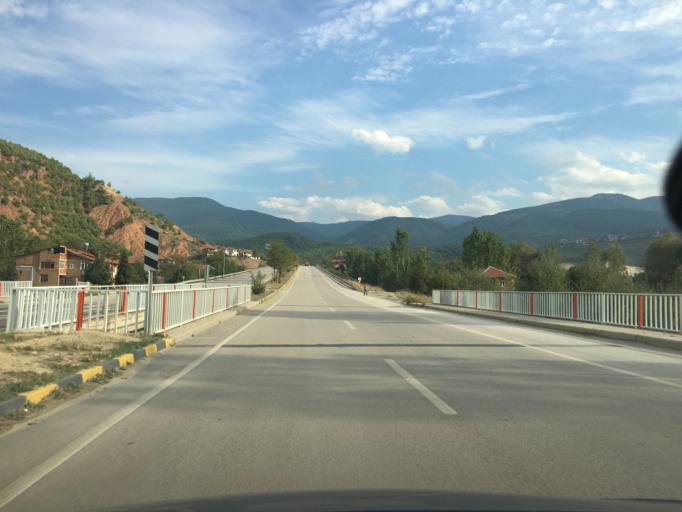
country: TR
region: Karabuk
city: Karabuk
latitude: 41.0997
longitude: 32.6716
